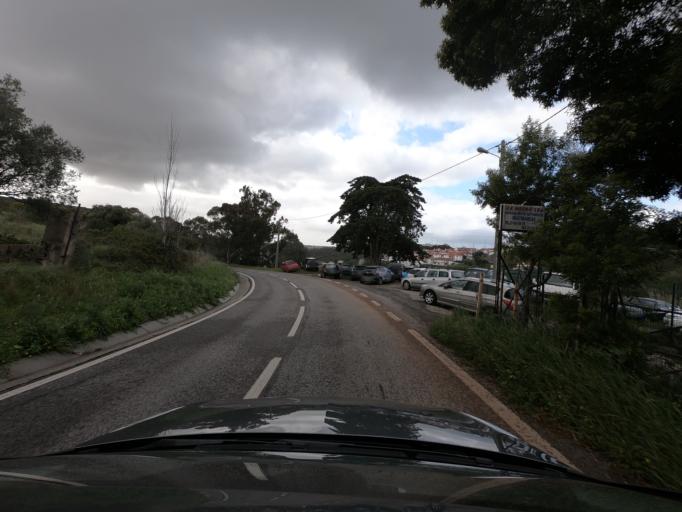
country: PT
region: Lisbon
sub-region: Sintra
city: Queluz
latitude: 38.7405
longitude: -9.2631
